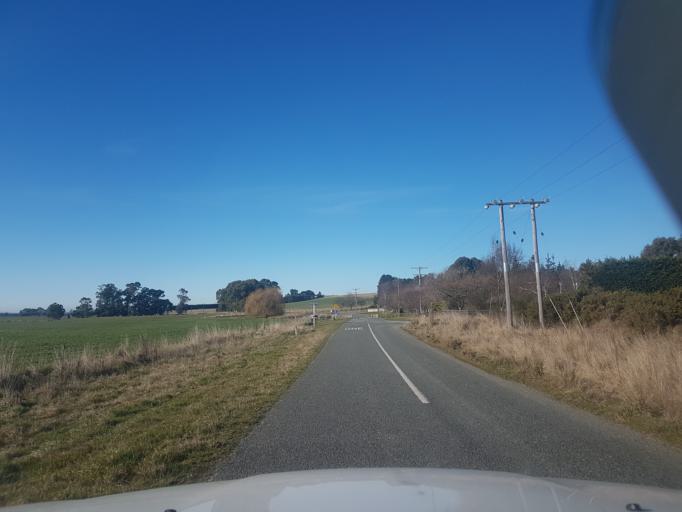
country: NZ
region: Canterbury
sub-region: Timaru District
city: Pleasant Point
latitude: -44.2882
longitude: 171.0790
